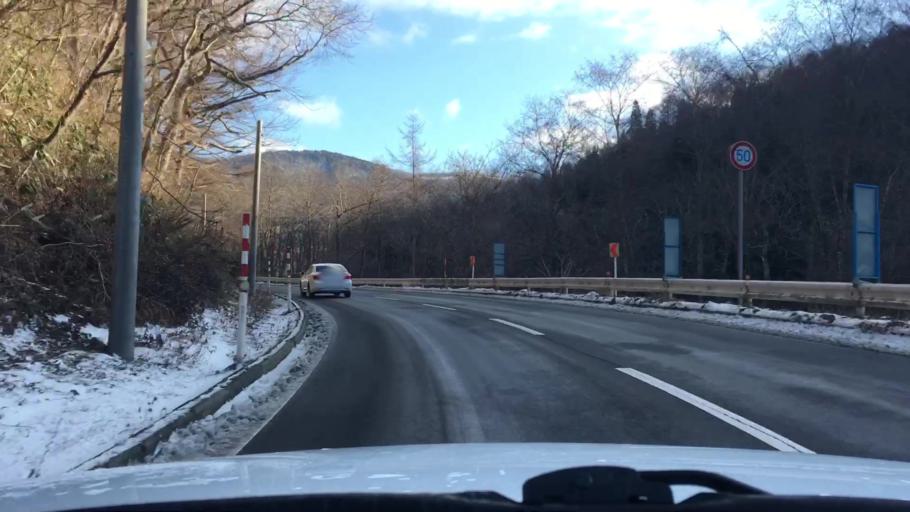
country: JP
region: Iwate
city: Morioka-shi
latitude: 39.6669
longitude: 141.3215
